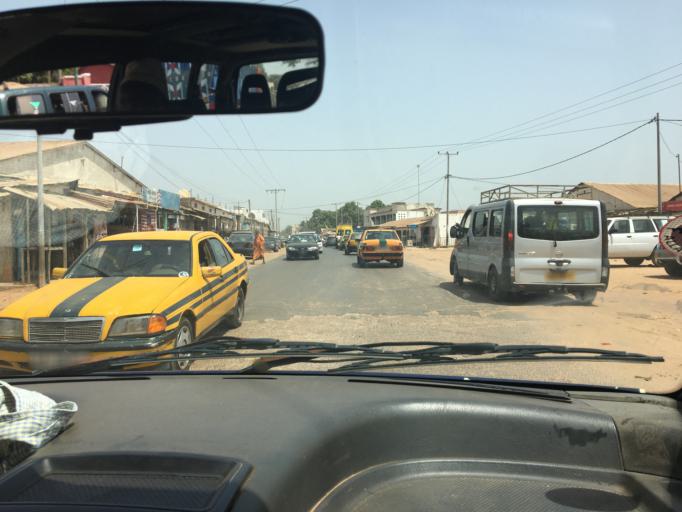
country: GM
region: Western
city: Abuko
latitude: 13.3970
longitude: -16.6734
